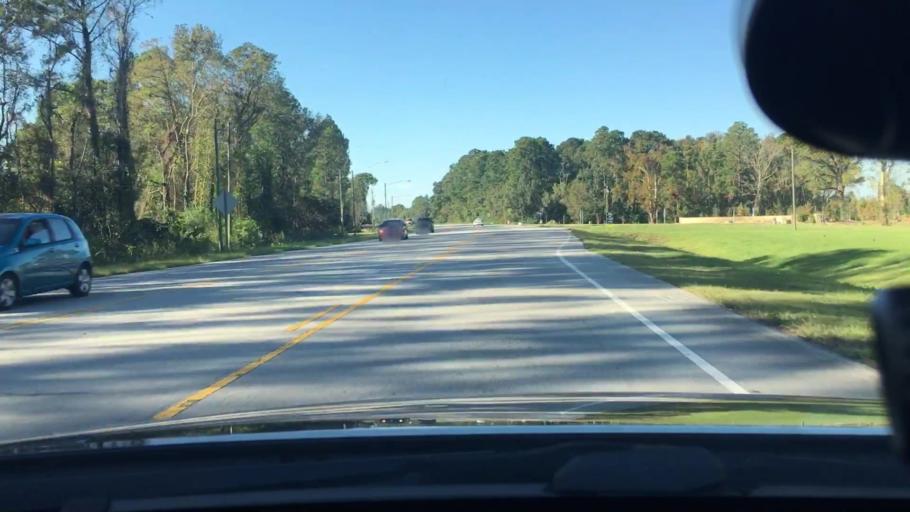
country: US
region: North Carolina
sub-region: Craven County
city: Trent Woods
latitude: 35.1505
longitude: -77.1092
